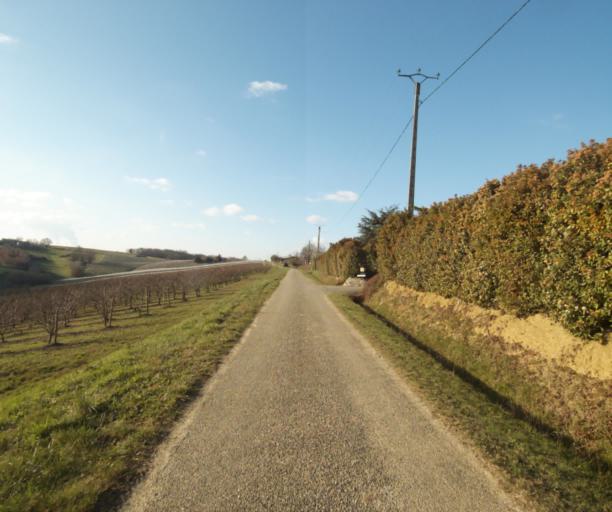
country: FR
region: Midi-Pyrenees
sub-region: Departement du Tarn-et-Garonne
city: Saint-Nicolas-de-la-Grave
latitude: 44.1238
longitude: 1.0309
